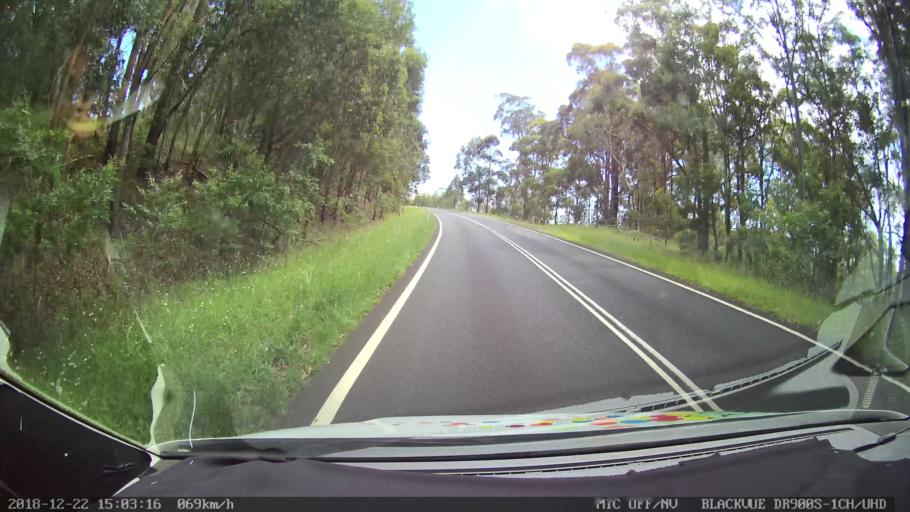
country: AU
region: New South Wales
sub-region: Bellingen
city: Dorrigo
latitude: -30.2630
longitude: 152.4420
